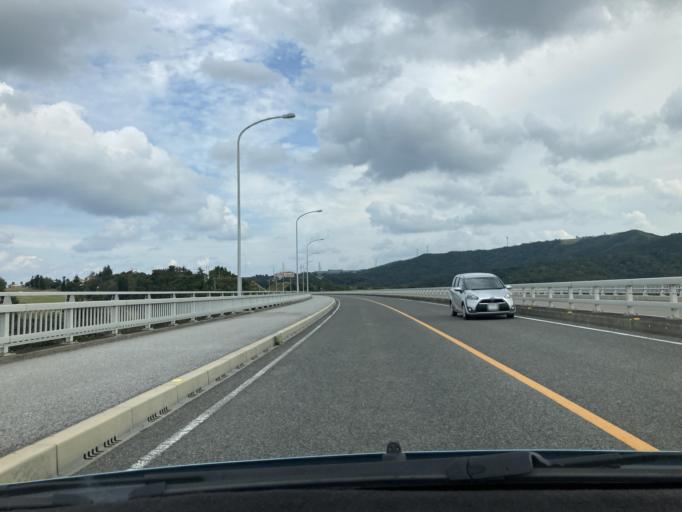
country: JP
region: Okinawa
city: Ishikawa
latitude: 26.4489
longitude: 127.8163
